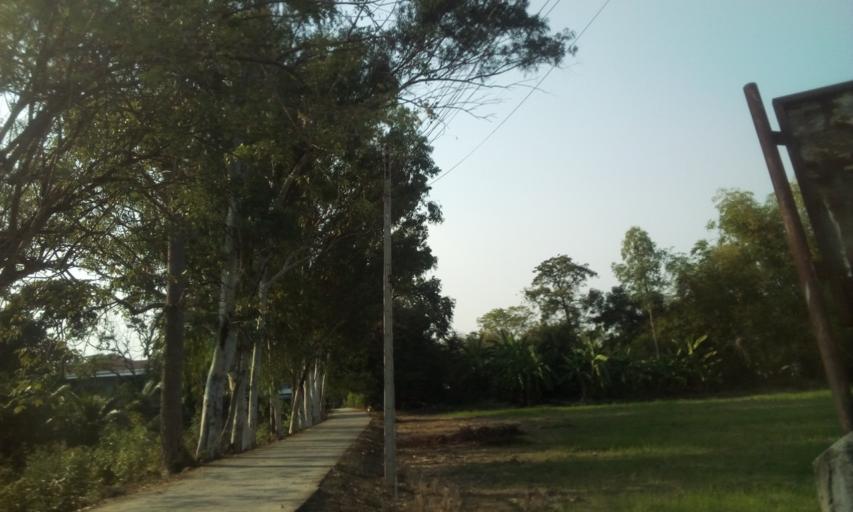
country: TH
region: Sing Buri
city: Sing Buri
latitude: 14.8356
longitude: 100.4012
